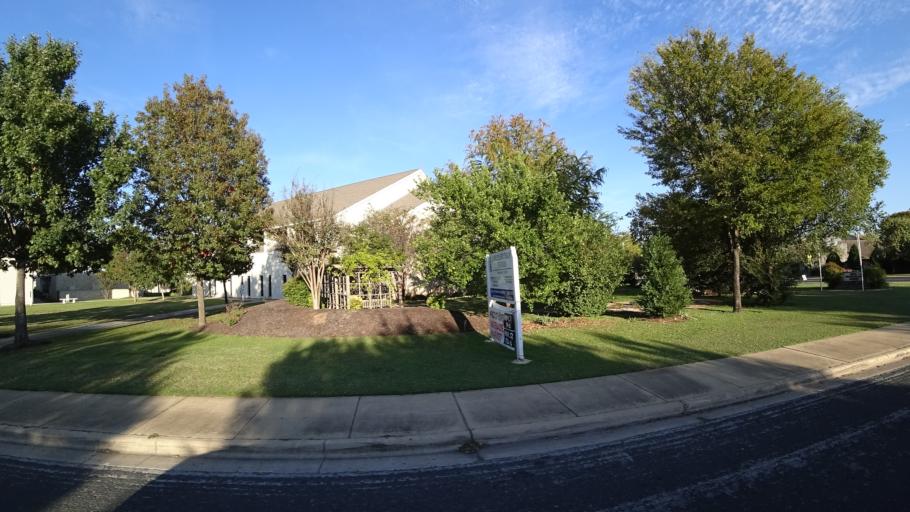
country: US
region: Texas
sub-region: Williamson County
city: Anderson Mill
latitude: 30.4448
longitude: -97.8065
